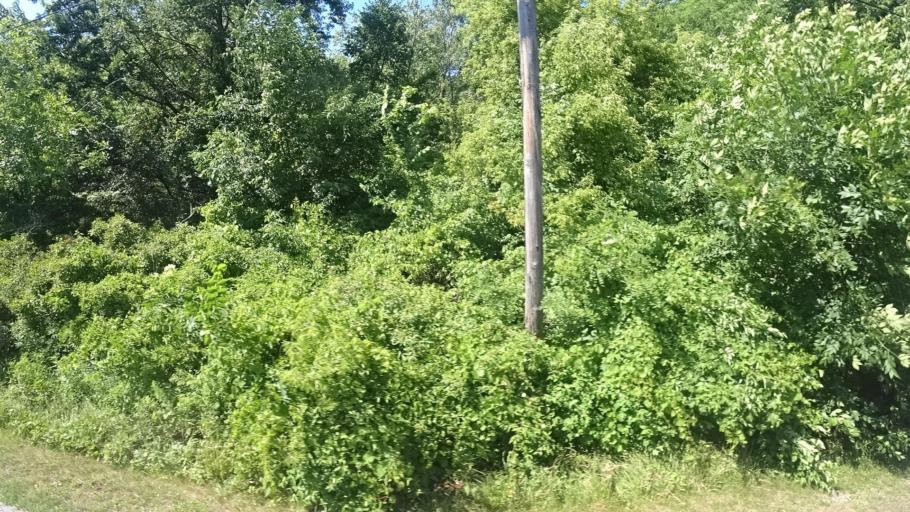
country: US
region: Indiana
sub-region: Porter County
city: Burns Harbor
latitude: 41.5981
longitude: -87.1369
